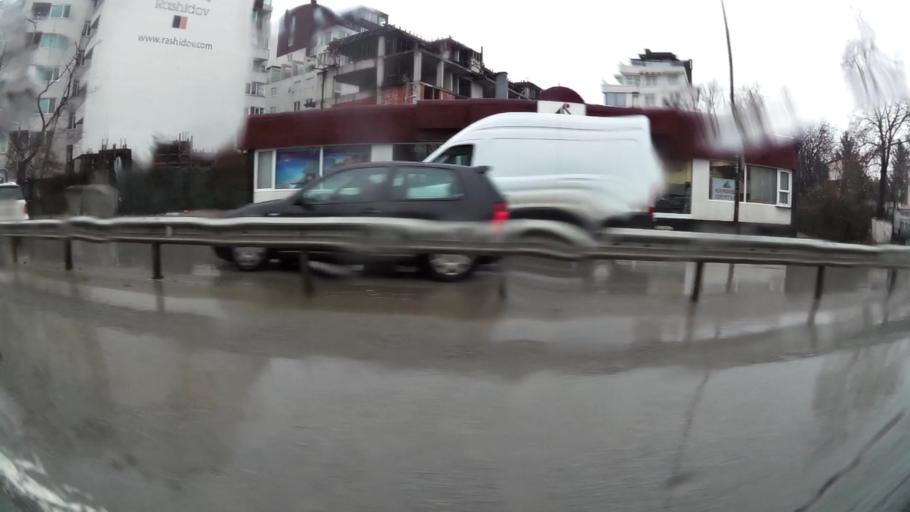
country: BG
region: Sofia-Capital
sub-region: Stolichna Obshtina
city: Sofia
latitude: 42.6556
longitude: 23.3362
